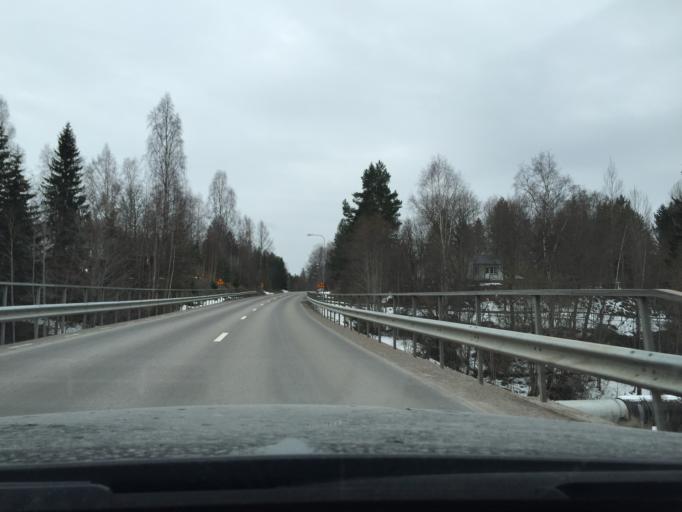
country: SE
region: Gaevleborg
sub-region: Sandvikens Kommun
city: Jarbo
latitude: 60.7582
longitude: 16.5353
